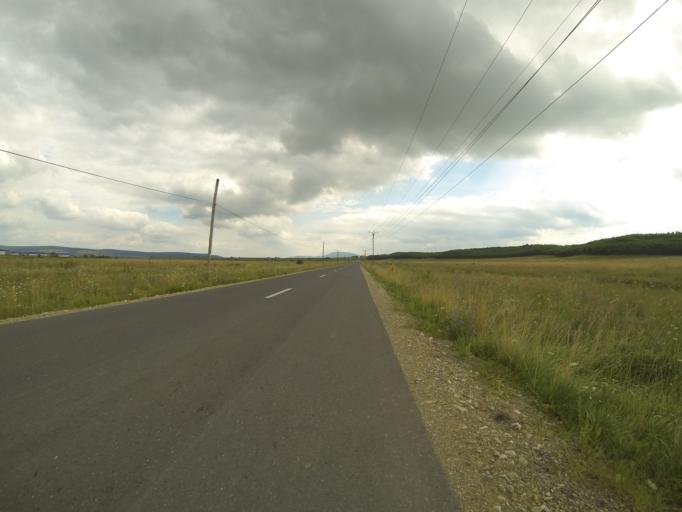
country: RO
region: Brasov
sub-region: Comuna Sercaia
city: Sercaia
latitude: 45.8334
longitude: 25.1545
